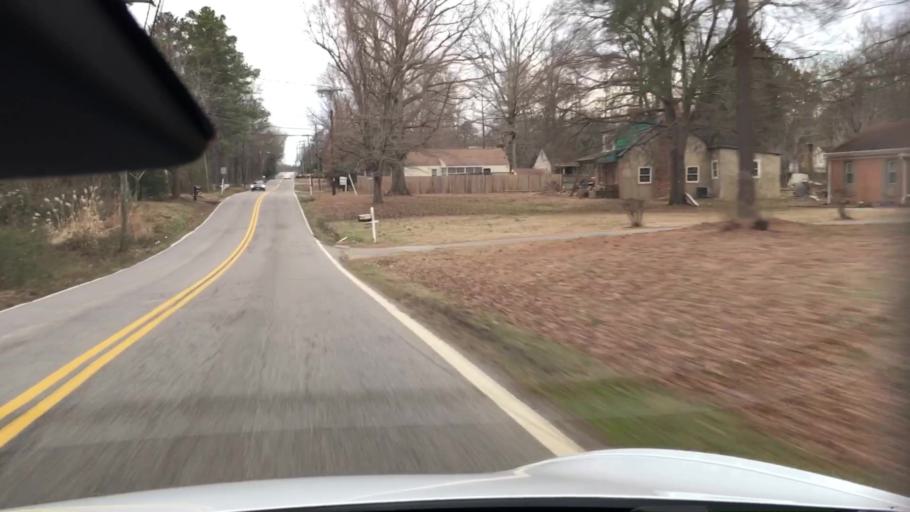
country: US
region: Virginia
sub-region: Chesterfield County
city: Bon Air
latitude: 37.5145
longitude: -77.5767
